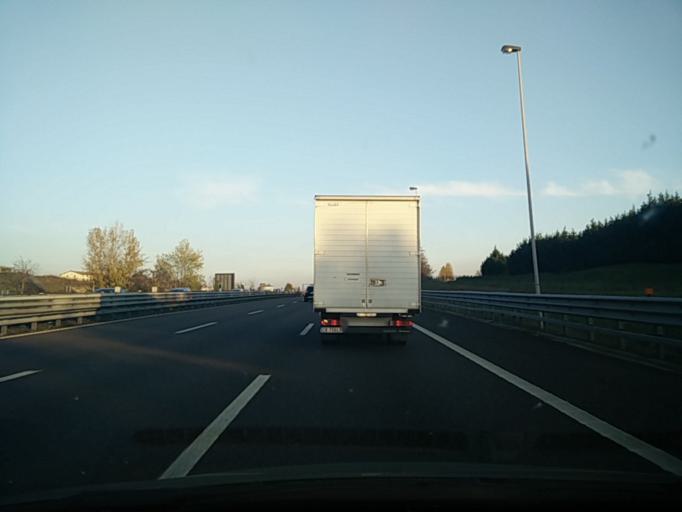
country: IT
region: Veneto
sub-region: Provincia di Verona
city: Cavalcaselle
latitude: 45.4293
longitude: 10.7117
